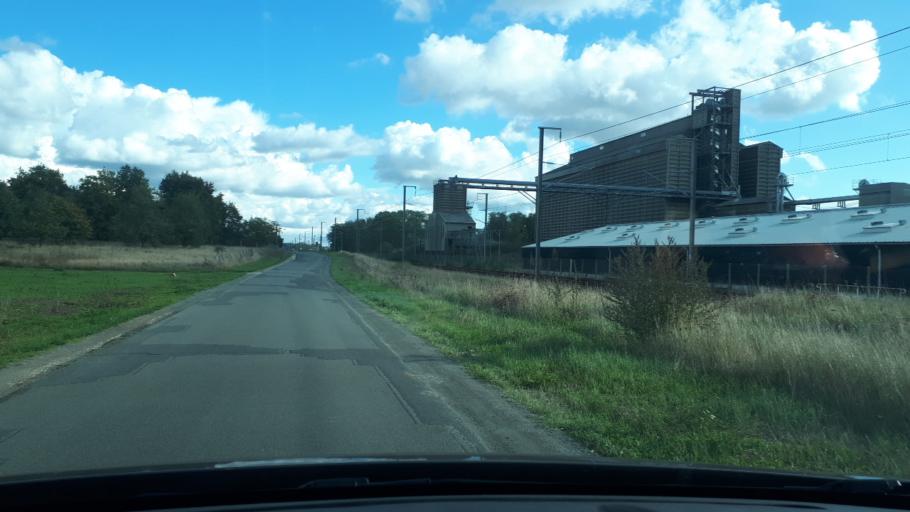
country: FR
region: Centre
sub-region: Departement du Loir-et-Cher
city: Saint-Aignan
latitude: 47.2957
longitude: 1.3649
